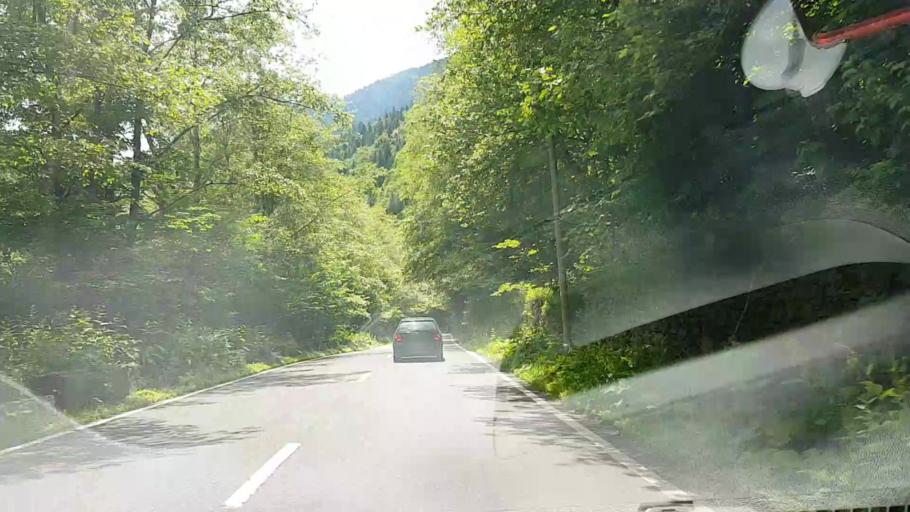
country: RO
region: Suceava
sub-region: Comuna Crucea
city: Crucea
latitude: 47.2959
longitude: 25.6323
